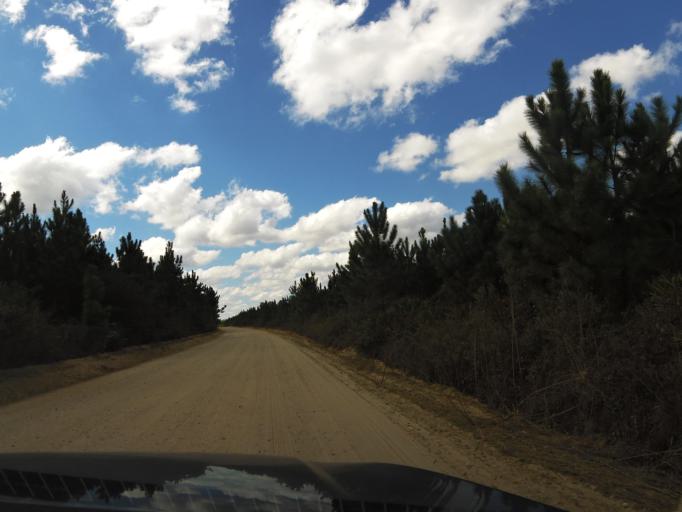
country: US
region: Florida
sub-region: Clay County
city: Keystone Heights
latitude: 29.8211
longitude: -81.8321
